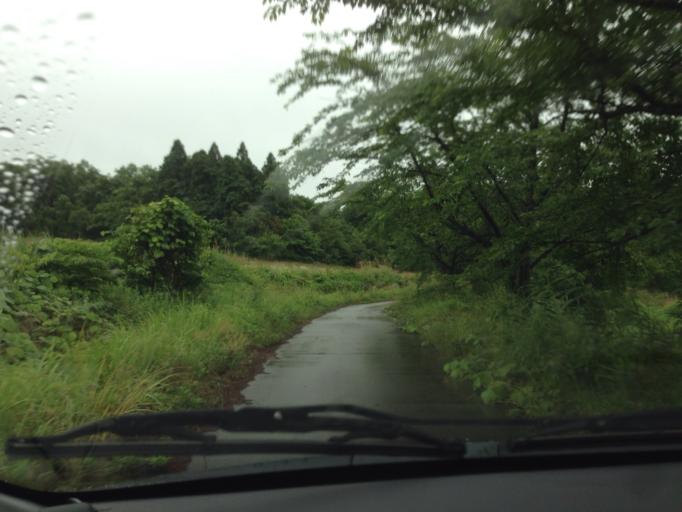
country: JP
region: Fukushima
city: Kitakata
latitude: 37.5663
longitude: 139.9724
